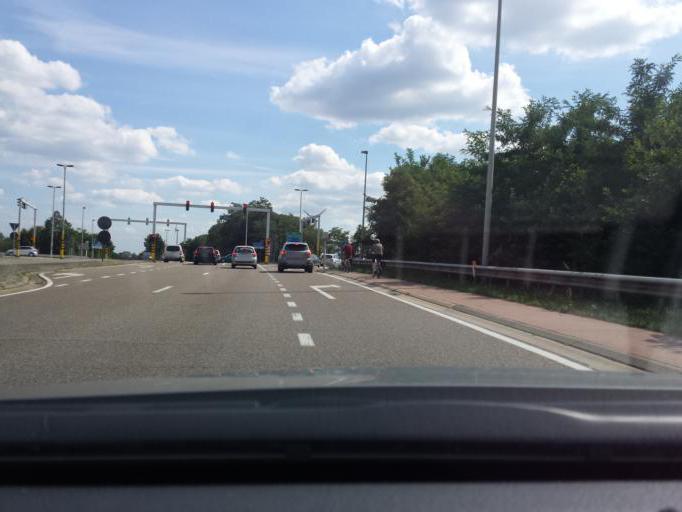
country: BE
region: Flanders
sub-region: Provincie Limburg
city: Beringen
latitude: 51.0463
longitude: 5.2185
